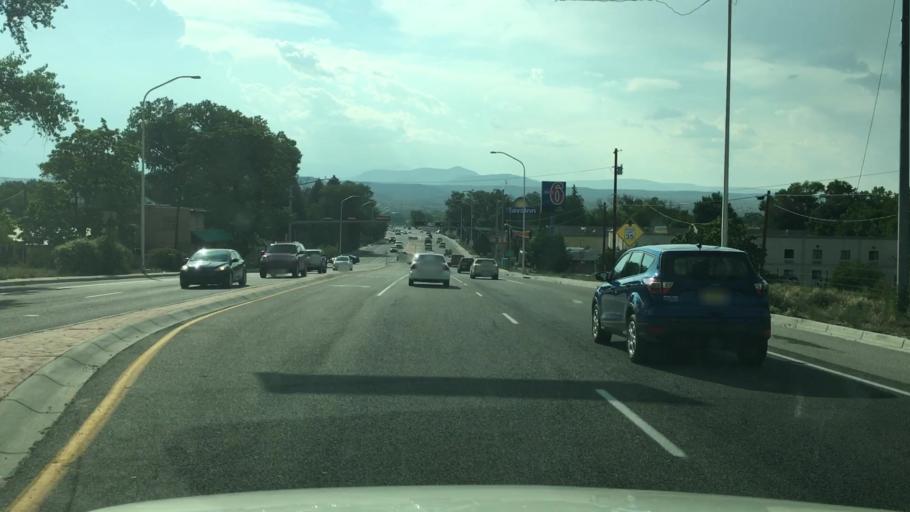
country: US
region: New Mexico
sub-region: Rio Arriba County
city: Espanola
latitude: 35.9866
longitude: -106.0567
